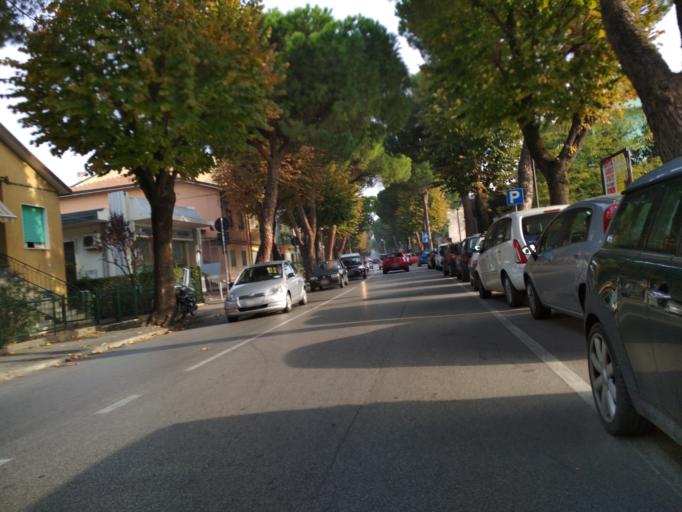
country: IT
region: Emilia-Romagna
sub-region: Provincia di Rimini
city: Rimini
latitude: 44.0703
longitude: 12.5650
